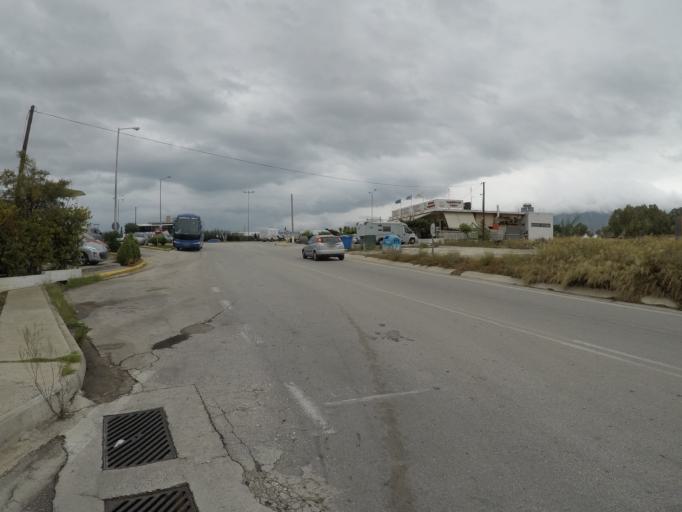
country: GR
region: Peloponnese
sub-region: Nomos Korinthias
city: Kyras Vrysi
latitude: 37.9257
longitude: 22.9946
